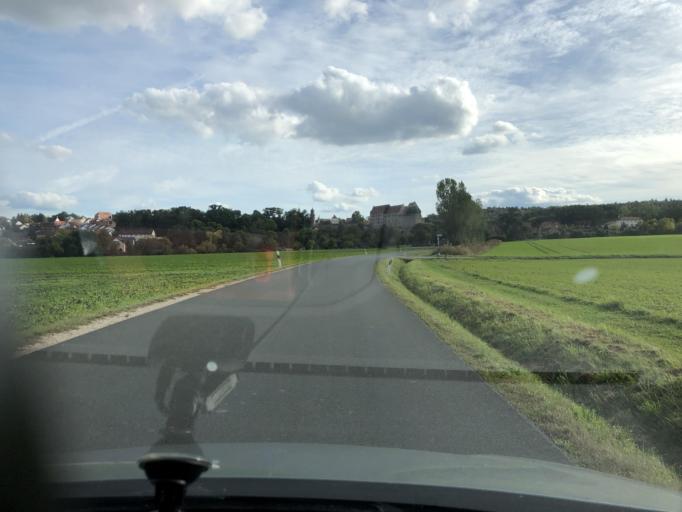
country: DE
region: Bavaria
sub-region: Regierungsbezirk Mittelfranken
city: Cadolzburg
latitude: 49.4660
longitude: 10.8490
